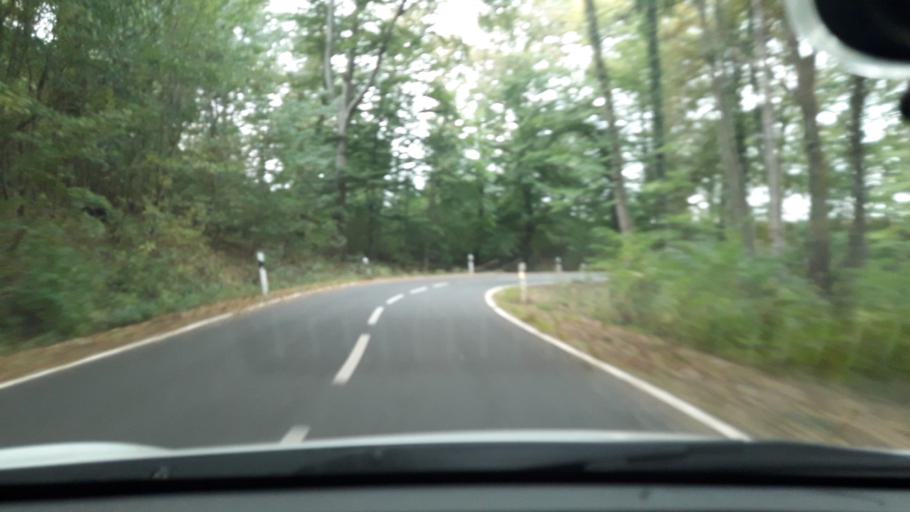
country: DE
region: Lower Saxony
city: Gielde
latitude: 52.0512
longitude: 10.4876
